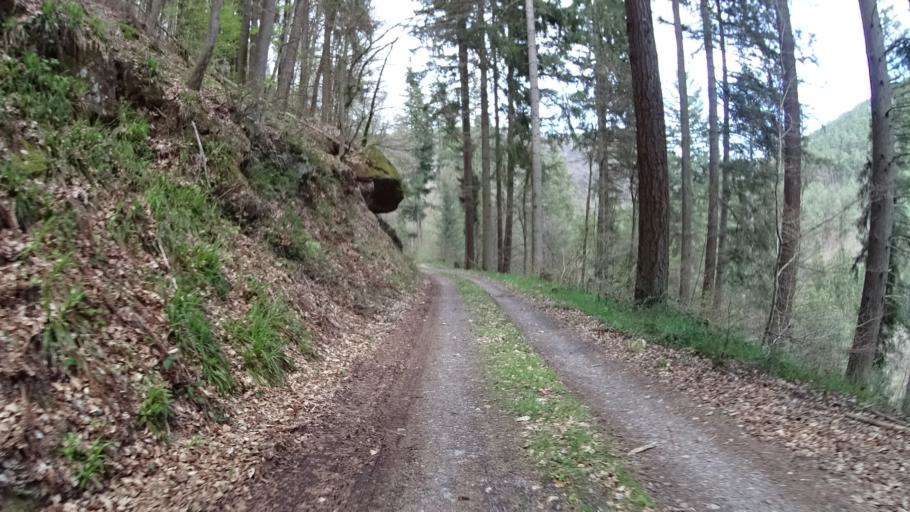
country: DE
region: Rheinland-Pfalz
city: Esthal
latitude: 49.3400
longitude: 7.9994
